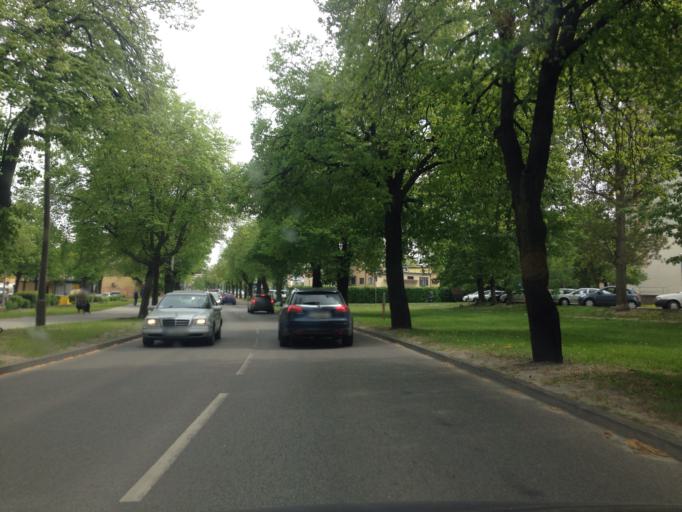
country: PL
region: Pomeranian Voivodeship
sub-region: Sopot
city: Sopot
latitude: 54.4220
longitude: 18.5806
